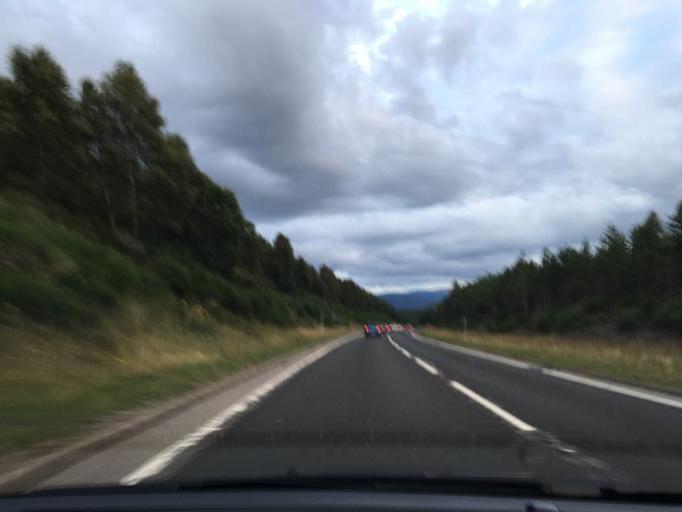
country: GB
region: Scotland
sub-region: Highland
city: Aviemore
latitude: 57.2893
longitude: -3.8463
